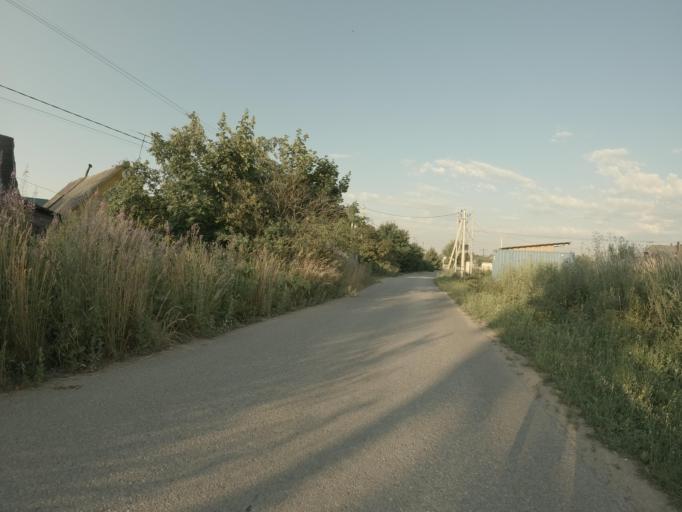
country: RU
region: Leningrad
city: Koltushi
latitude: 59.8891
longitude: 30.6978
